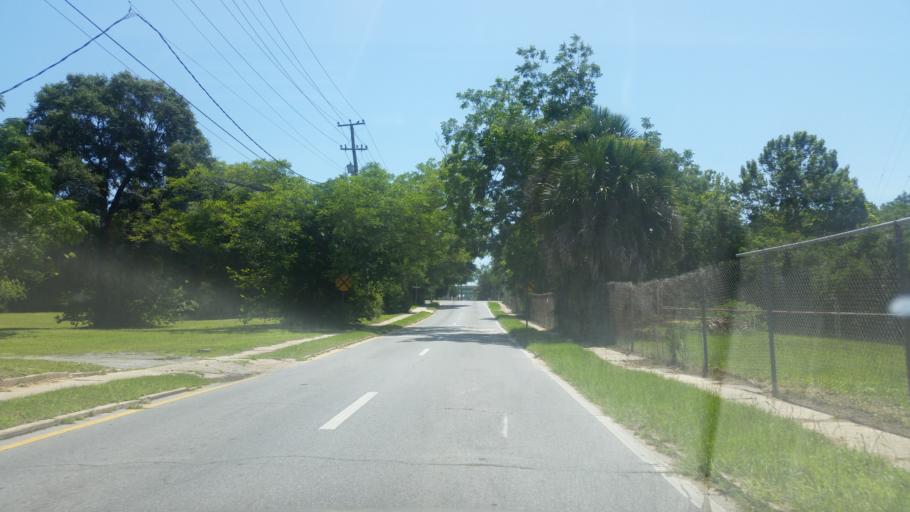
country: US
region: Florida
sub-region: Escambia County
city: Goulding
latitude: 30.4337
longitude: -87.2195
